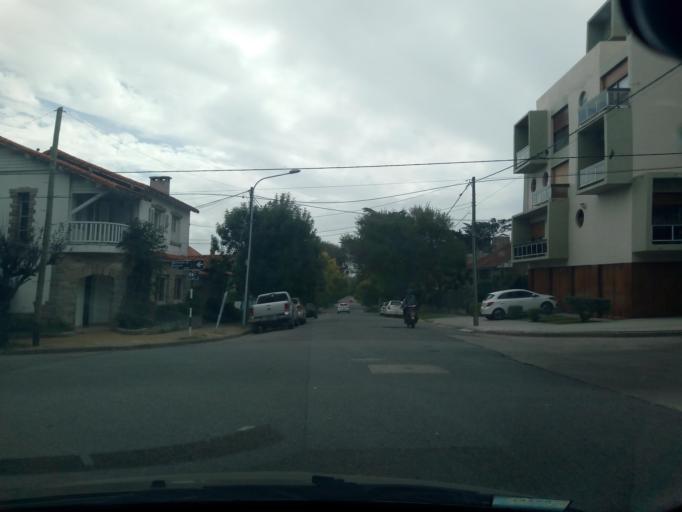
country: AR
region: Buenos Aires
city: Mar del Plata
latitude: -38.0255
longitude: -57.5354
